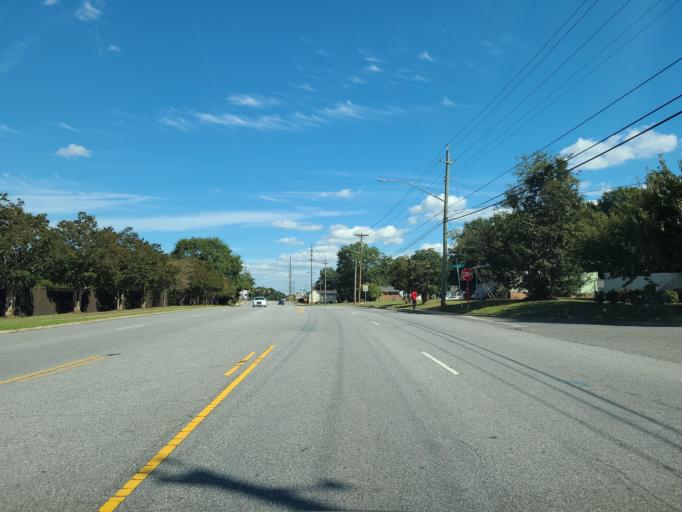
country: US
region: North Carolina
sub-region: Gaston County
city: Gastonia
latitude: 35.2578
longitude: -81.2108
